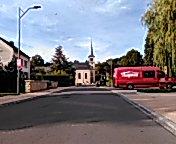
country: LU
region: Luxembourg
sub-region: Canton de Capellen
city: Steinfort
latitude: 49.6451
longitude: 5.9157
